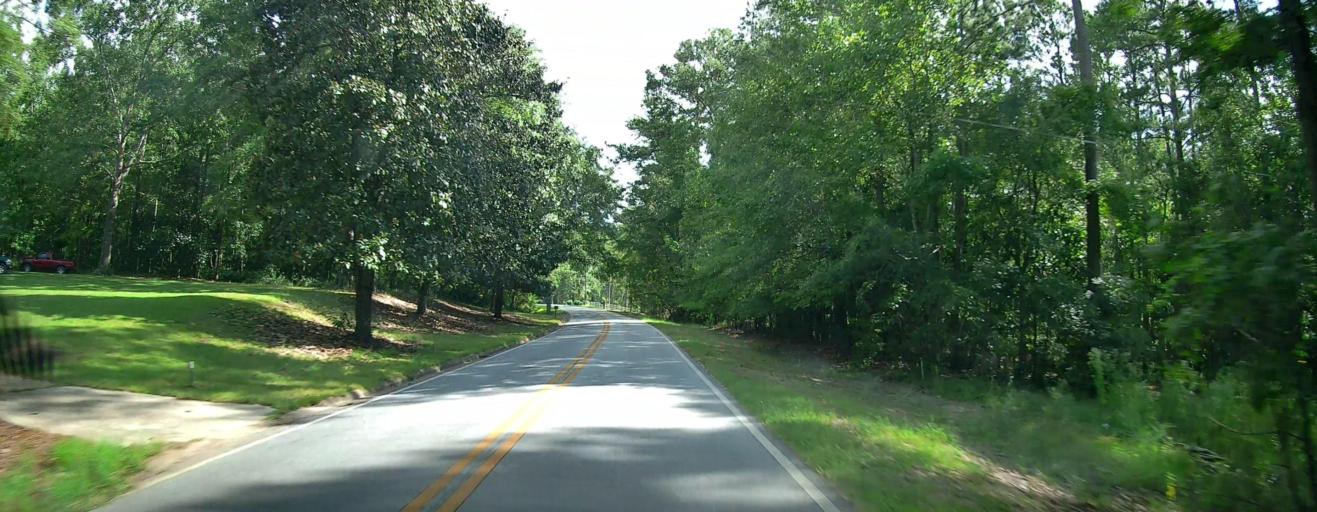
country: US
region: Alabama
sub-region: Lee County
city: Smiths Station
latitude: 32.6061
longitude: -84.9819
